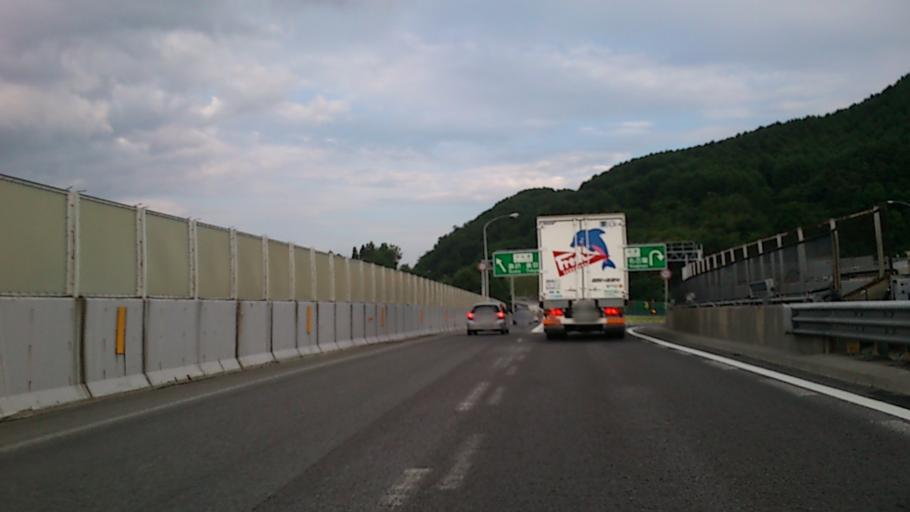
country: JP
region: Nagano
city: Okaya
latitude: 36.0546
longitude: 138.0426
